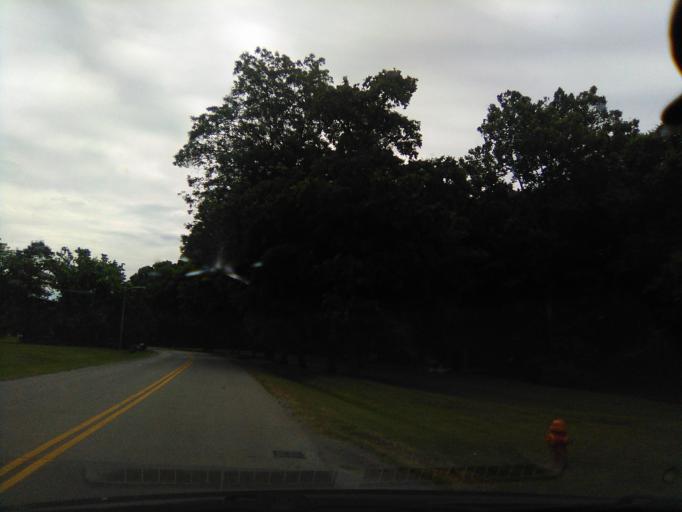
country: US
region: Tennessee
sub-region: Davidson County
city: Belle Meade
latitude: 36.1034
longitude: -86.8885
